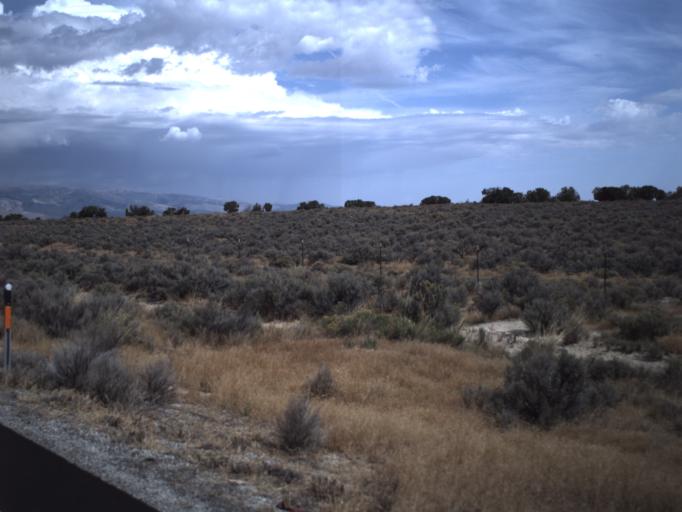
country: US
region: Idaho
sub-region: Cassia County
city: Burley
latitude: 41.7041
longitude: -113.5324
